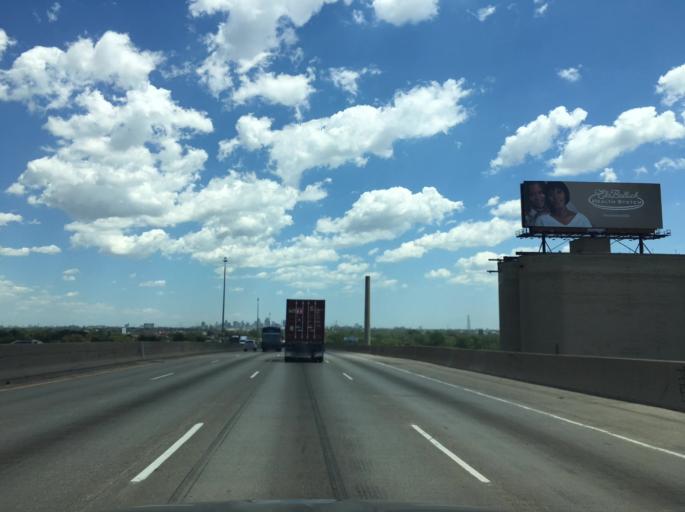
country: US
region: Michigan
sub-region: Wayne County
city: River Rouge
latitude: 42.2872
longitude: -83.1387
